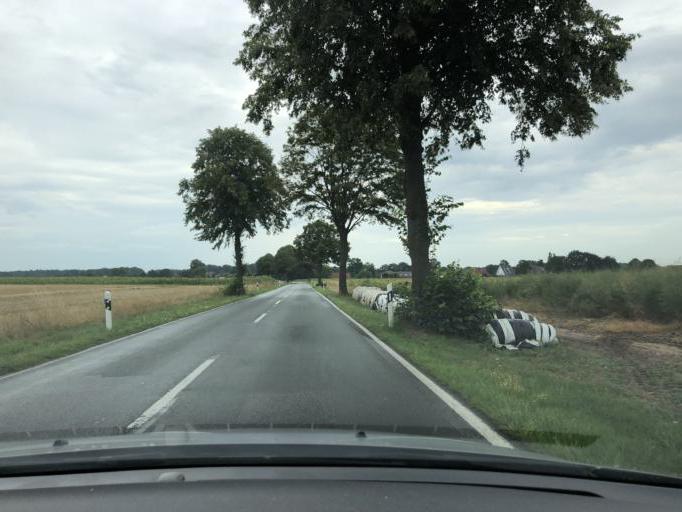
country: DE
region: North Rhine-Westphalia
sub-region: Regierungsbezirk Dusseldorf
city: Schermbeck
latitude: 51.6519
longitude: 6.8931
